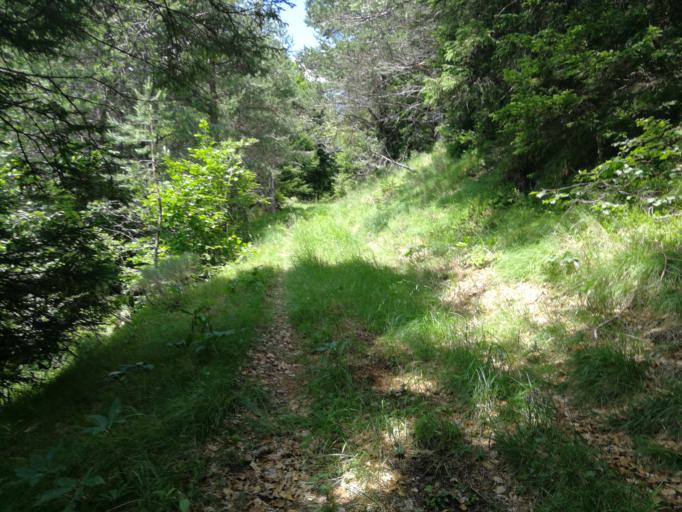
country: IT
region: Trentino-Alto Adige
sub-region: Provincia di Trento
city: Condino
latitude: 45.8616
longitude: 10.6170
